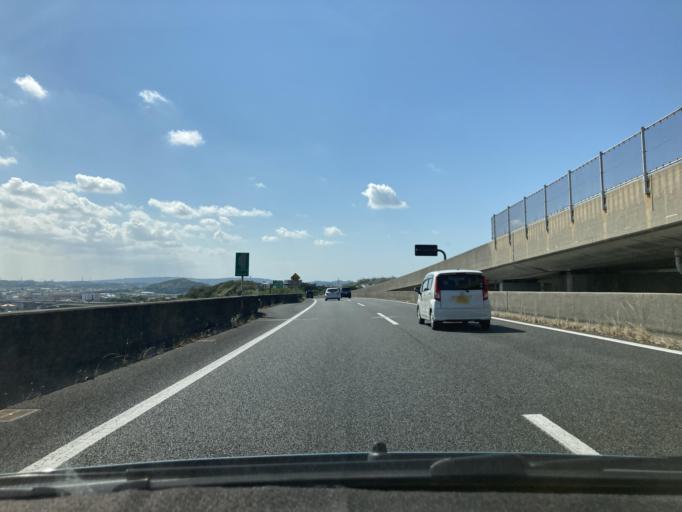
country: JP
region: Okinawa
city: Ginowan
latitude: 26.2134
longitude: 127.7385
